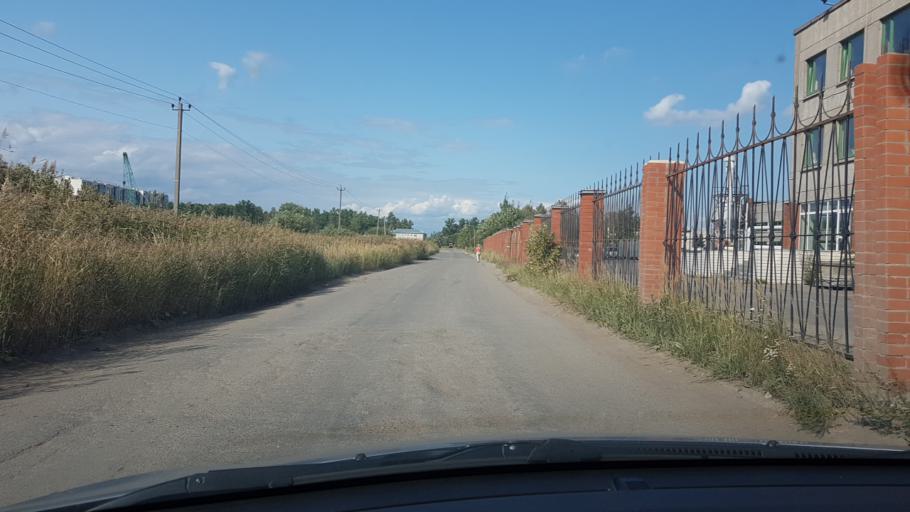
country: RU
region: St.-Petersburg
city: Sosnovaya Polyana
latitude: 59.8423
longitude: 30.1195
